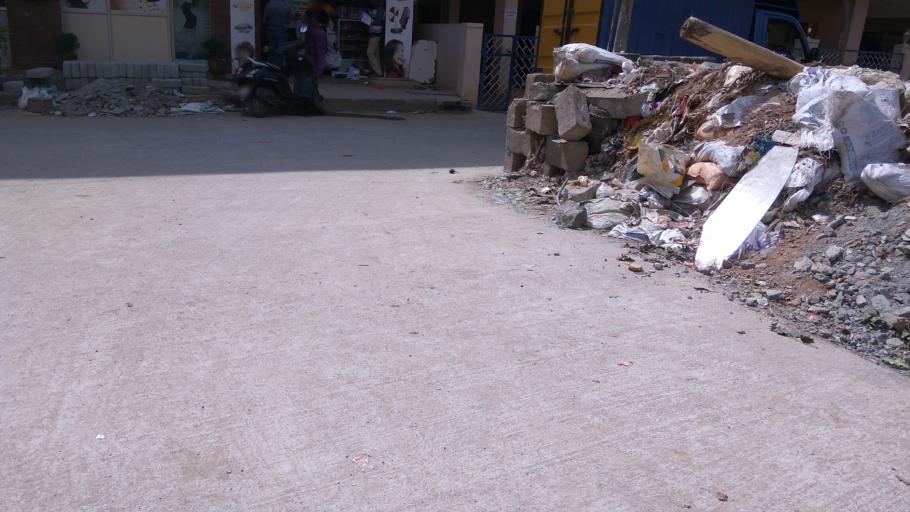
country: IN
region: Karnataka
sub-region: Bangalore Urban
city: Bangalore
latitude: 12.9547
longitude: 77.6934
